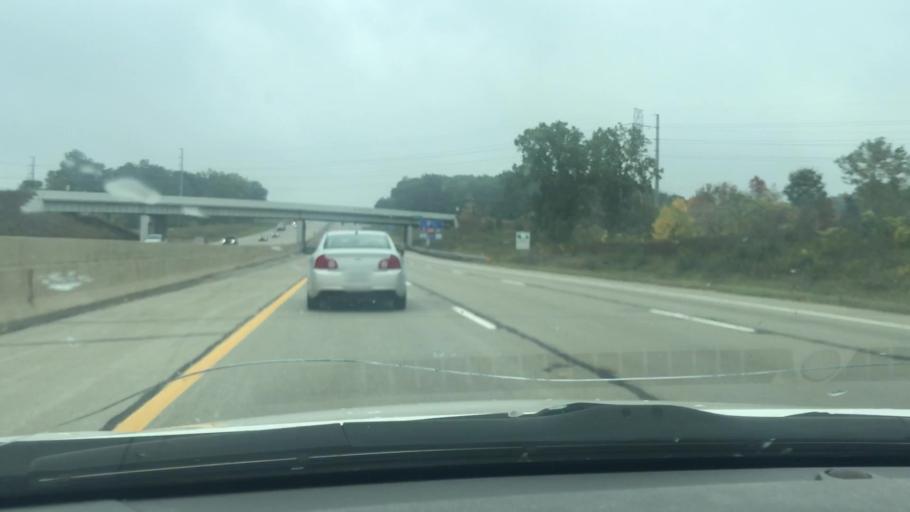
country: US
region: Michigan
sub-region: Livingston County
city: Howell
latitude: 42.5824
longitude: -83.8988
